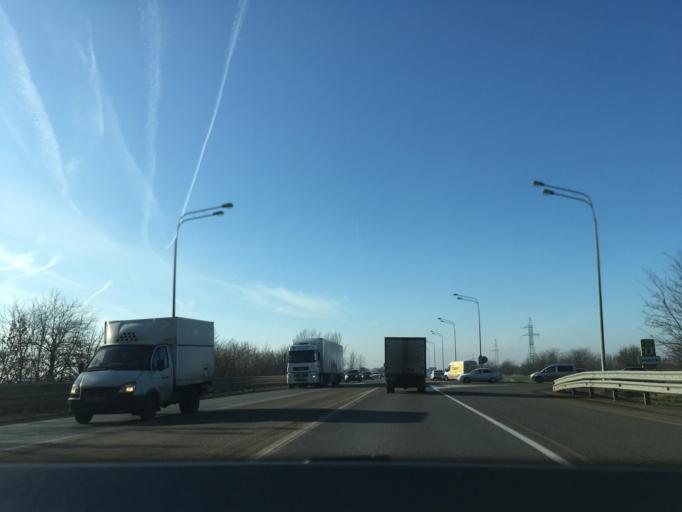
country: RU
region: Krasnodarskiy
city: Agronom
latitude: 45.1735
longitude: 39.0995
